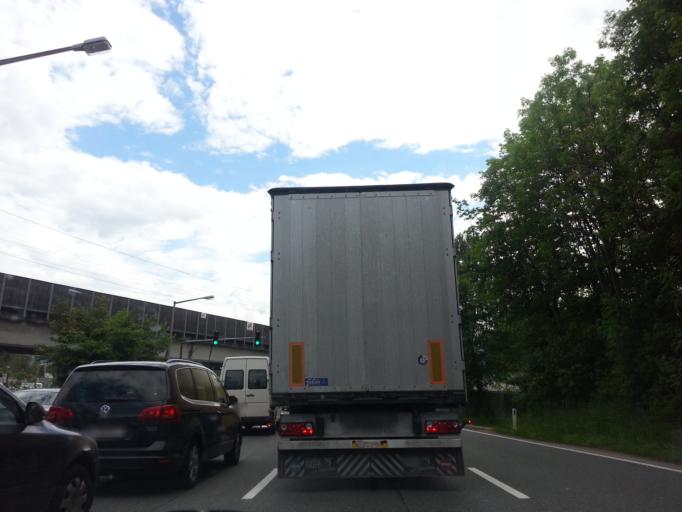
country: AT
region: Salzburg
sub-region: Politischer Bezirk Salzburg-Umgebung
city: Bergheim
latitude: 47.8265
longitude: 13.0539
